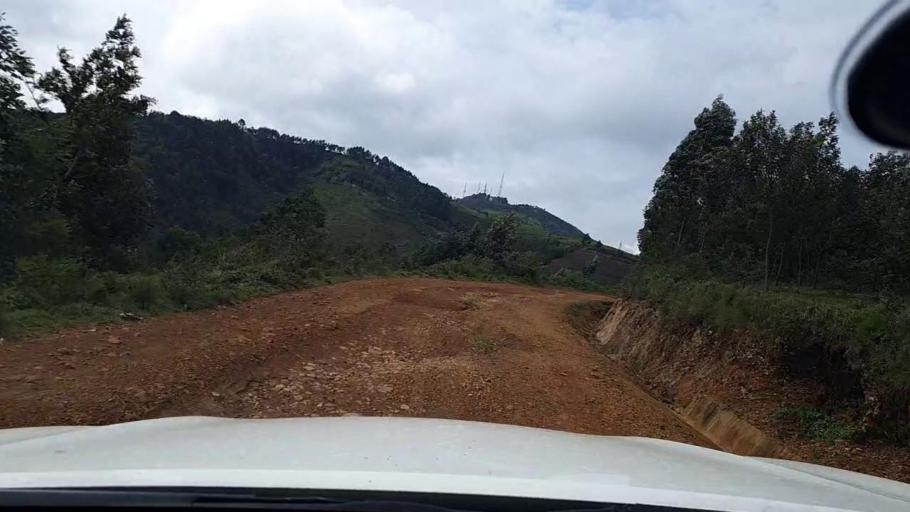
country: RW
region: Western Province
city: Kibuye
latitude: -2.1326
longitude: 29.3780
